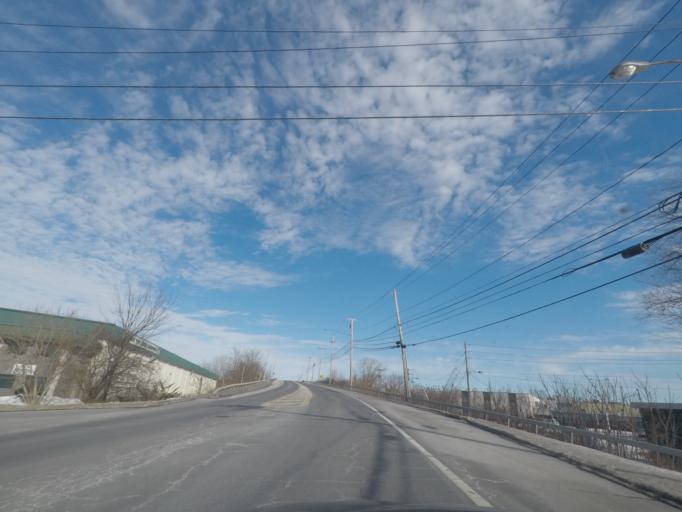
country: US
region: New York
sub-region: Schenectady County
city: Rotterdam
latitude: 42.7867
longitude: -73.9965
